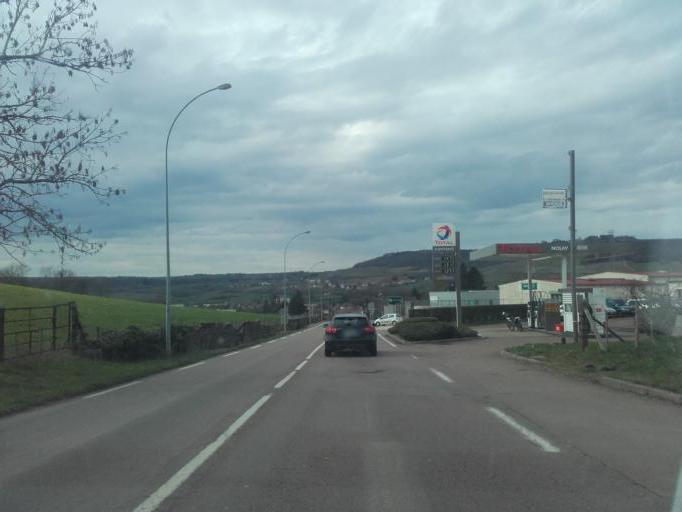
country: FR
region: Bourgogne
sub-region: Departement de la Cote-d'Or
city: Nolay
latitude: 46.9469
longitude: 4.6436
